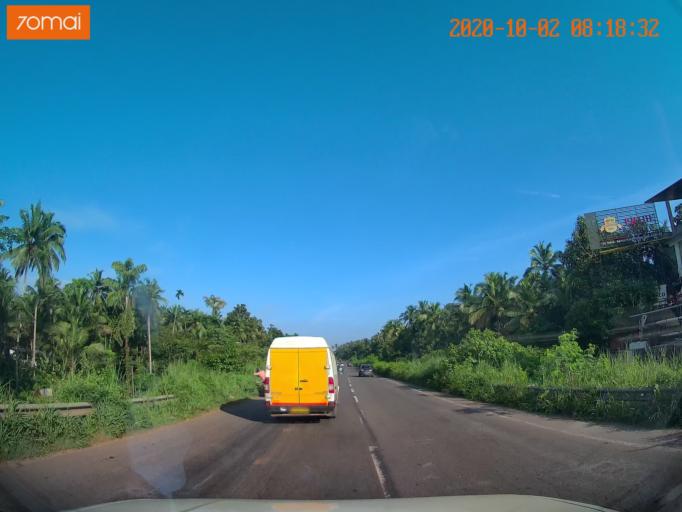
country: IN
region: Kerala
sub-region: Kozhikode
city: Kozhikode
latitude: 11.3034
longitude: 75.7906
